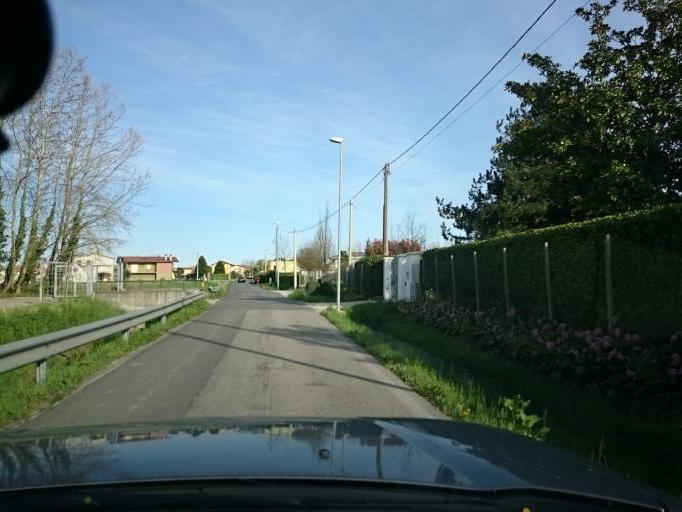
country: IT
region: Veneto
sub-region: Provincia di Padova
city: Mandriola-Sant'Agostino
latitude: 45.3678
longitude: 11.8620
